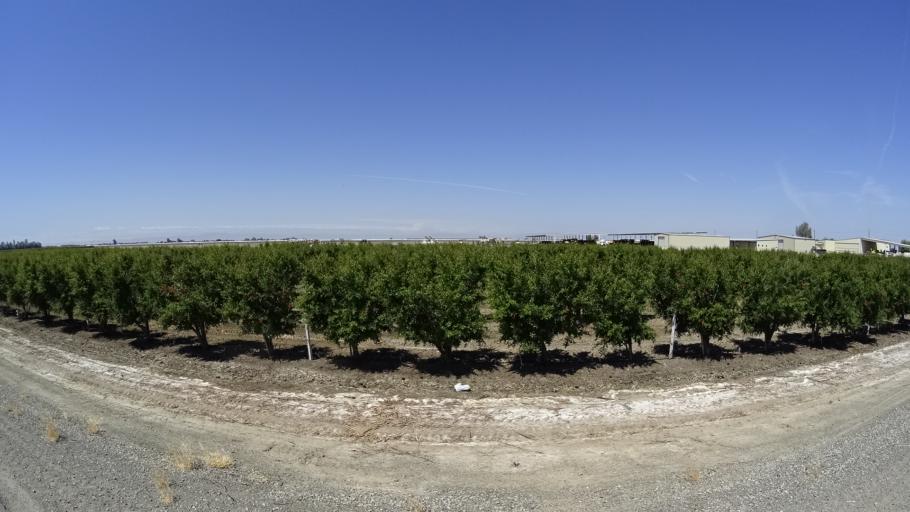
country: US
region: California
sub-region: Kings County
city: Stratford
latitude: 36.2233
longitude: -119.7982
